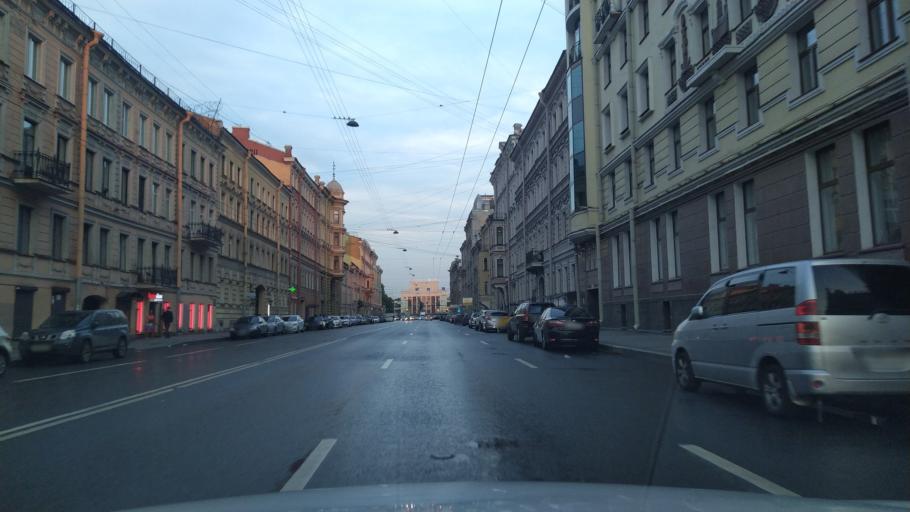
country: RU
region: St.-Petersburg
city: Saint Petersburg
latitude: 59.9238
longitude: 30.3290
